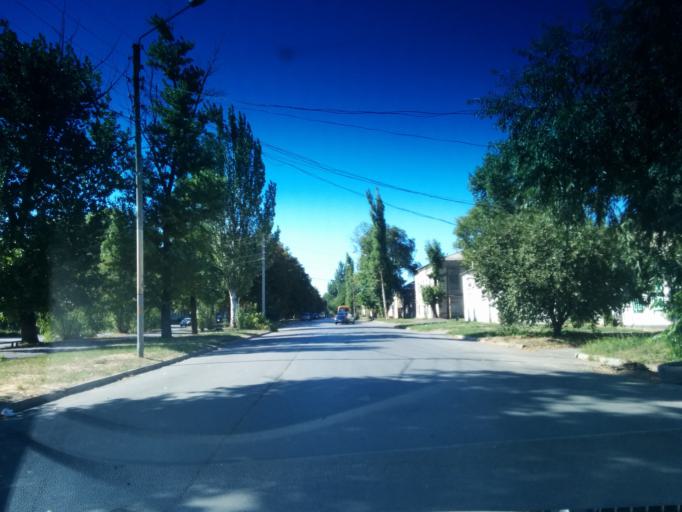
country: RU
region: Rostov
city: Shakhty
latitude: 47.7073
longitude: 40.2235
